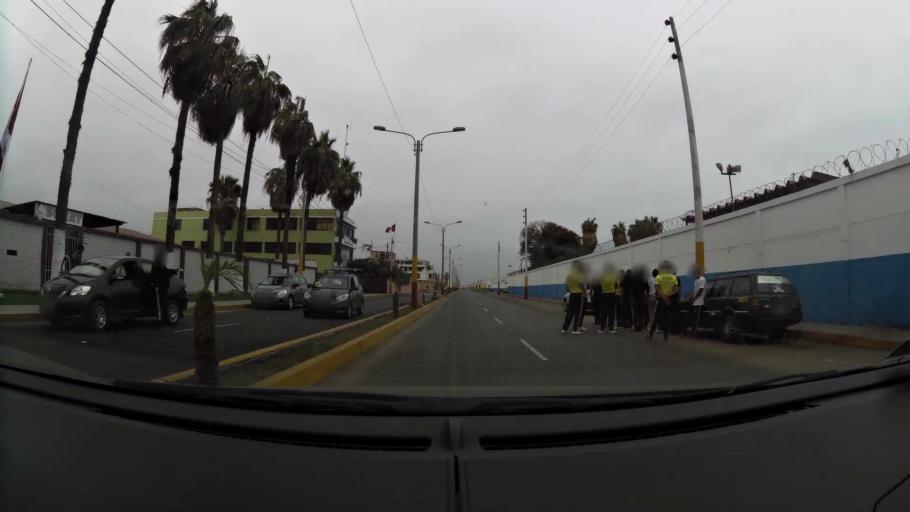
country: PE
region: Ancash
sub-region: Provincia de Santa
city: Chimbote
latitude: -9.0744
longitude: -78.6075
